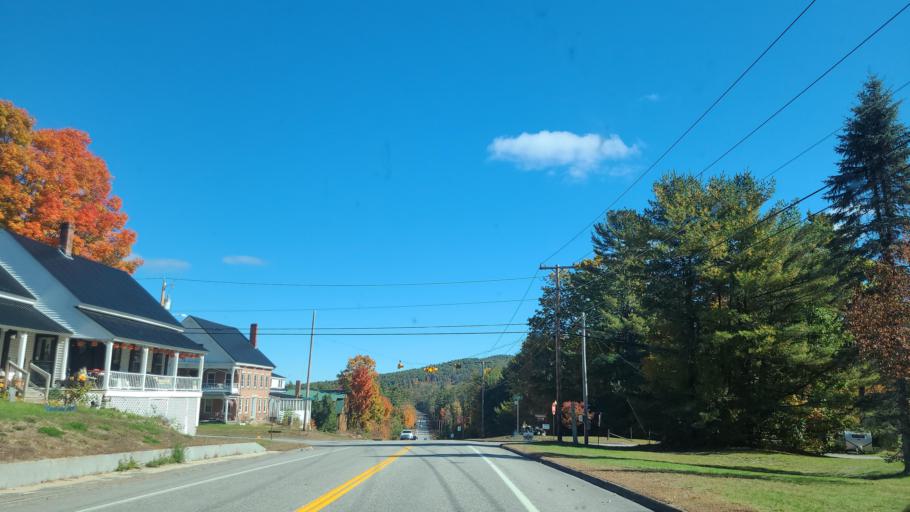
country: US
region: Maine
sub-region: Oxford County
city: Lovell
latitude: 44.0434
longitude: -70.8739
